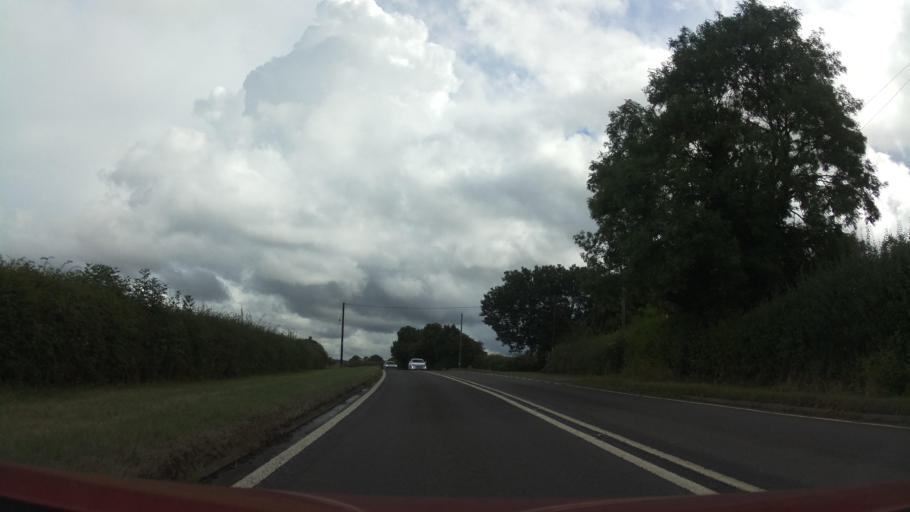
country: GB
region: England
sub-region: Shropshire
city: Bridgnorth
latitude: 52.5768
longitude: -2.3944
